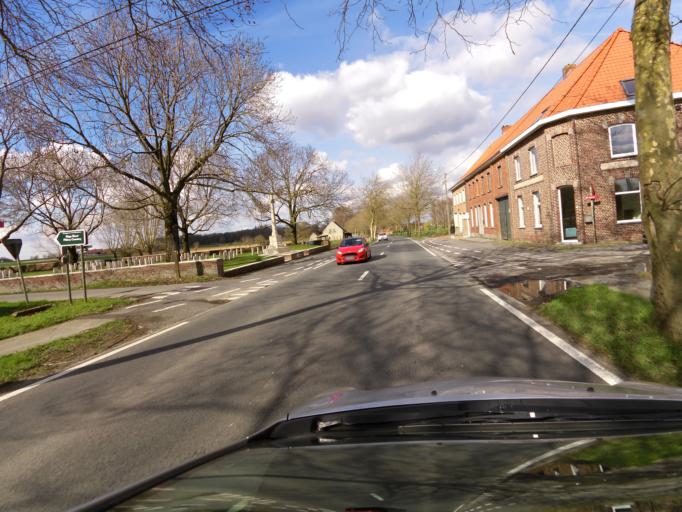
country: BE
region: Flanders
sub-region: Provincie West-Vlaanderen
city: Ieper
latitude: 50.8105
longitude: 2.8596
